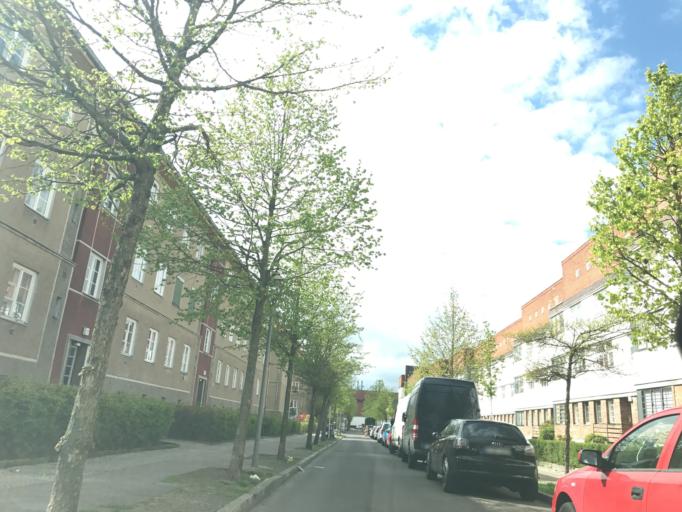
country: DE
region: Berlin
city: Reinickendorf
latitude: 52.5723
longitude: 13.3342
